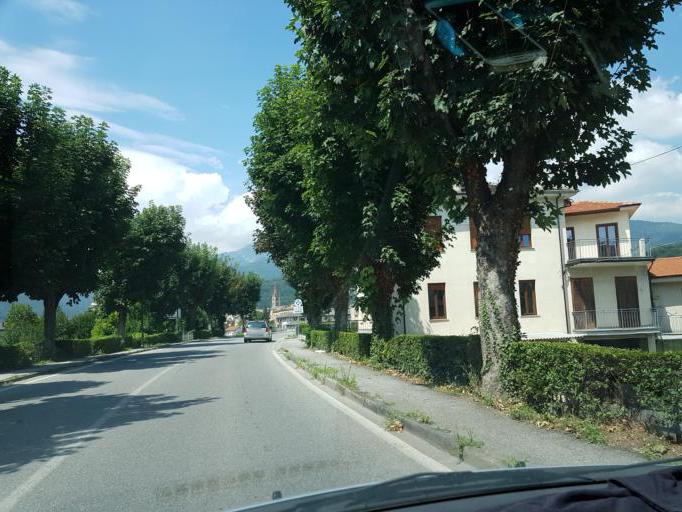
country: IT
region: Piedmont
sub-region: Provincia di Cuneo
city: Dronero
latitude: 44.4635
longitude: 7.3672
